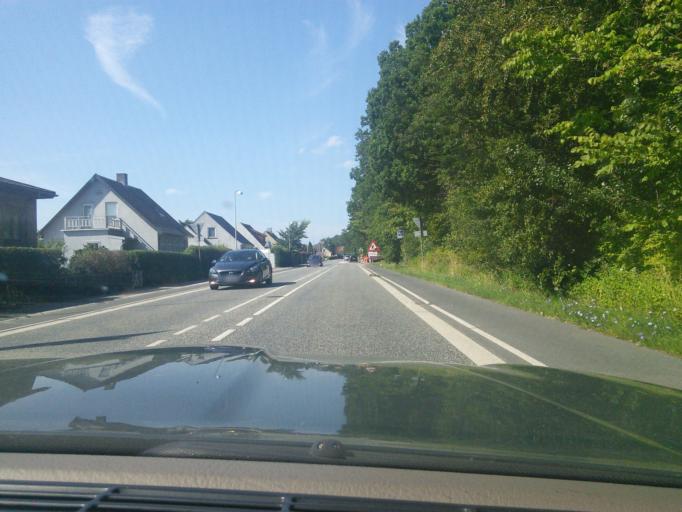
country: DK
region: Capital Region
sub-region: Halsnaes Kommune
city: Frederiksvaerk
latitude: 55.9832
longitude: 12.0199
